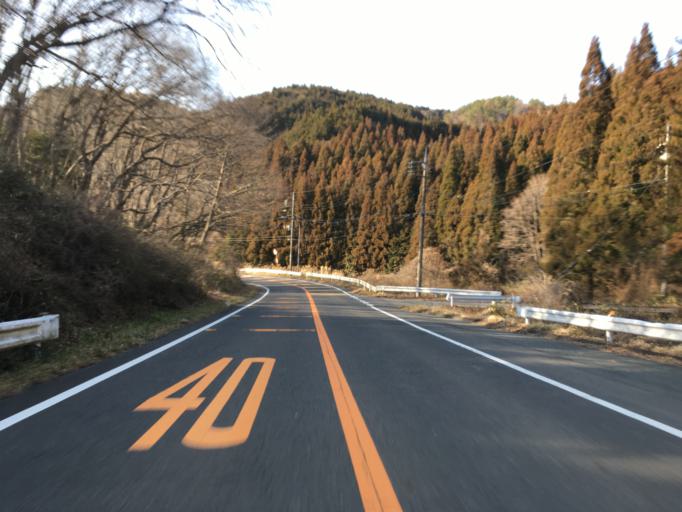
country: JP
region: Ibaraki
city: Hitachi
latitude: 36.7388
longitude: 140.5398
